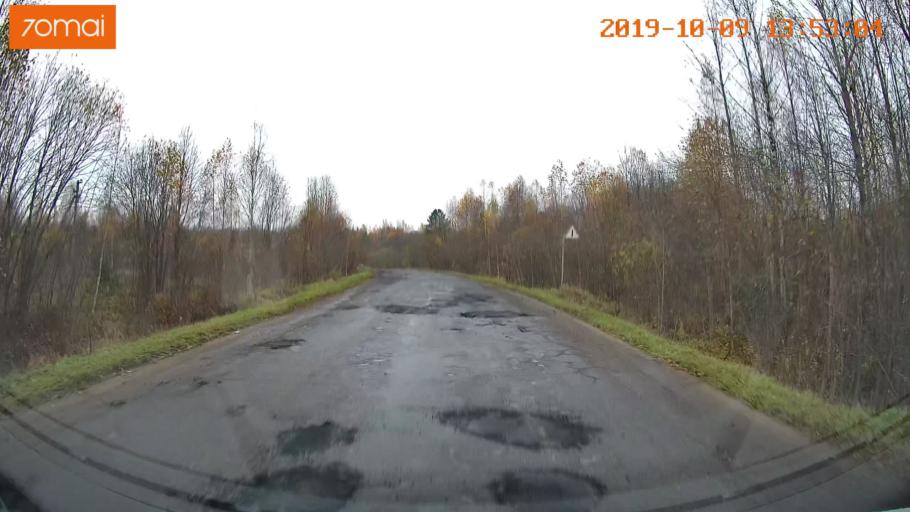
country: RU
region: Kostroma
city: Buy
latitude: 58.4136
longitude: 41.2546
